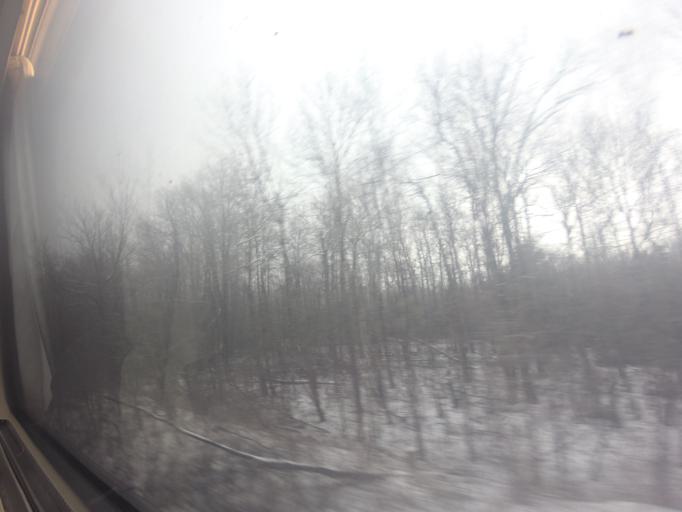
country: CA
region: Ontario
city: Cobourg
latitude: 43.9224
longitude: -78.4363
